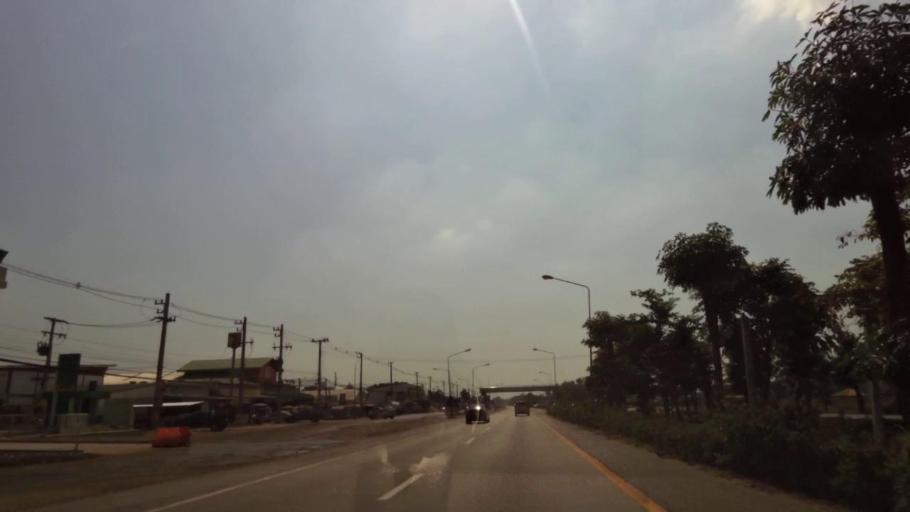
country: TH
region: Phichit
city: Wachira Barami
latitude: 16.5265
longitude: 100.1432
